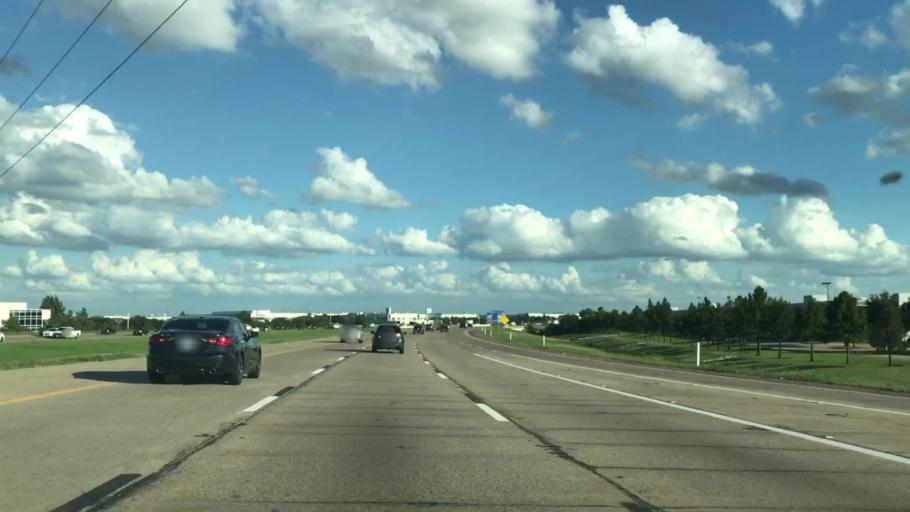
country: US
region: Texas
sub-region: Dallas County
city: Coppell
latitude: 32.9436
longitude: -97.0181
